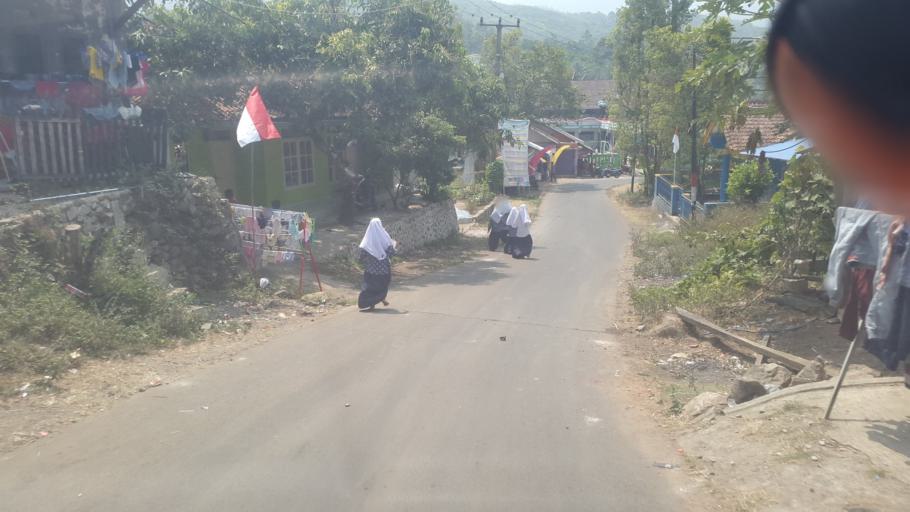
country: ID
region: West Java
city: Cimaja
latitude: -6.9219
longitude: 106.5231
